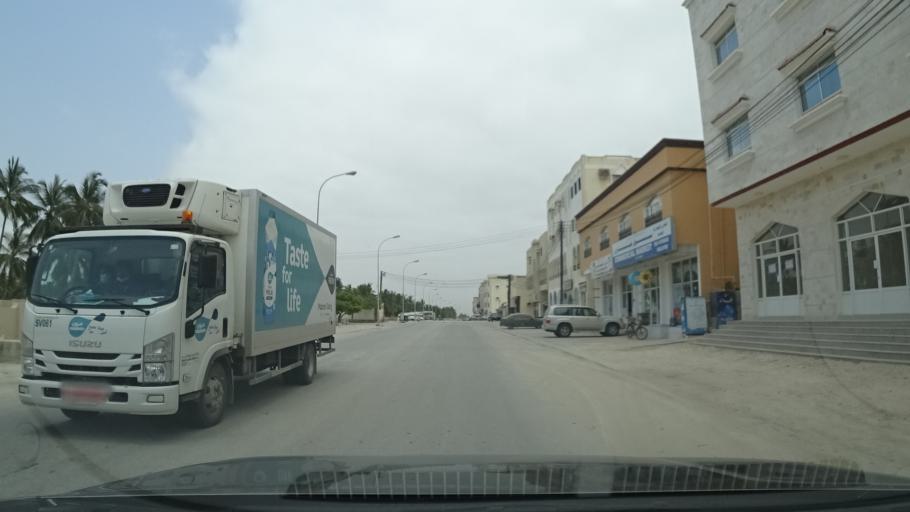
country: OM
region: Zufar
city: Salalah
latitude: 17.0225
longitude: 54.1619
